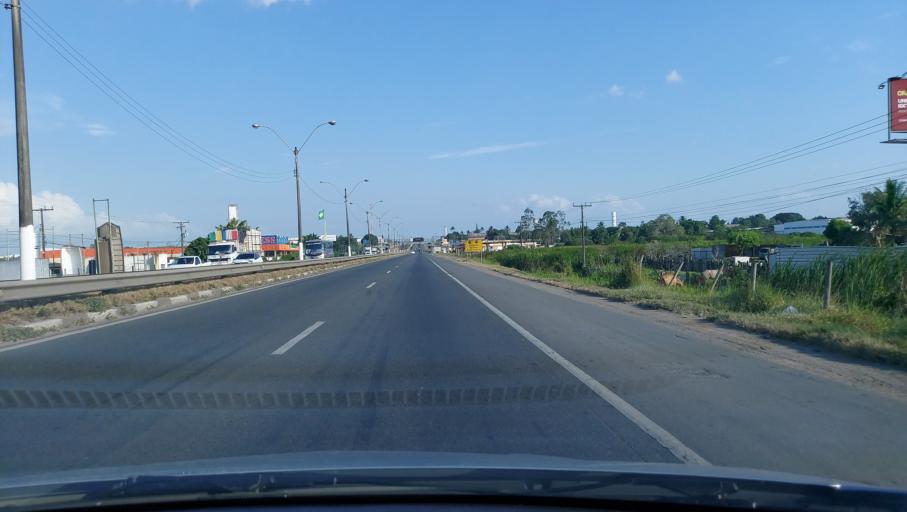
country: BR
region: Bahia
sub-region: Feira De Santana
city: Feira de Santana
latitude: -12.2762
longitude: -38.9304
